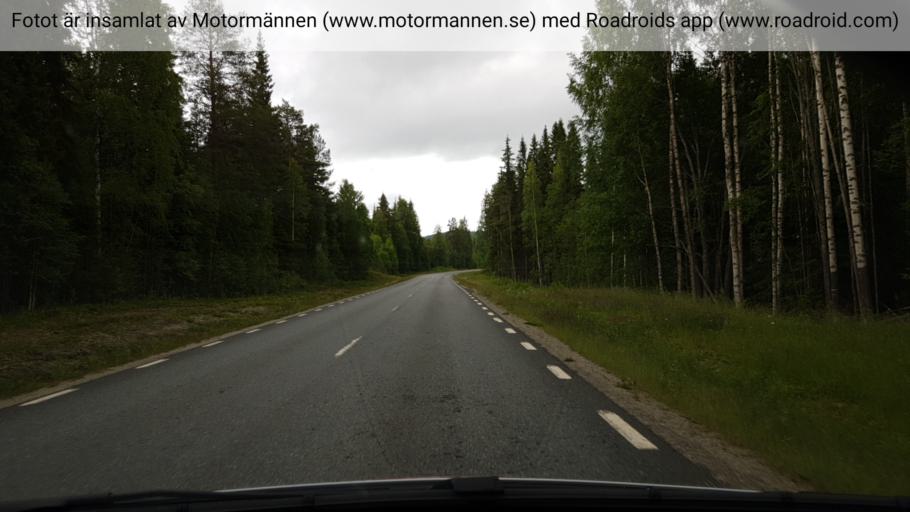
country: SE
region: Vaesterbotten
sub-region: Lycksele Kommun
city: Lycksele
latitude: 64.4488
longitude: 18.9366
